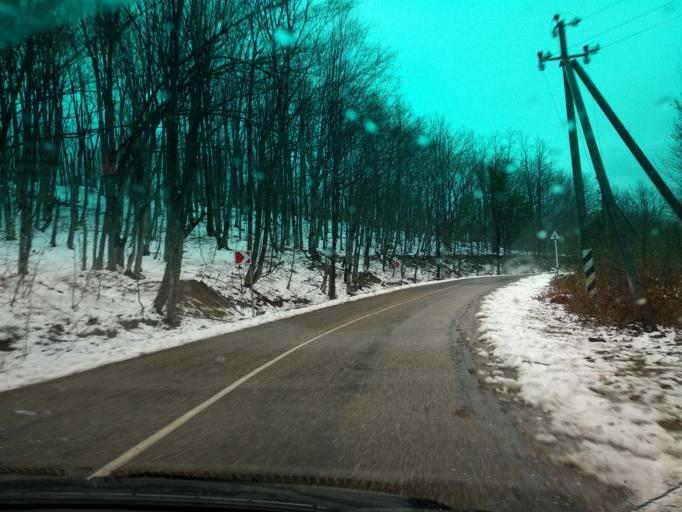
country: RU
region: Krasnodarskiy
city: Khadyzhensk
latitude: 44.2059
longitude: 39.3985
